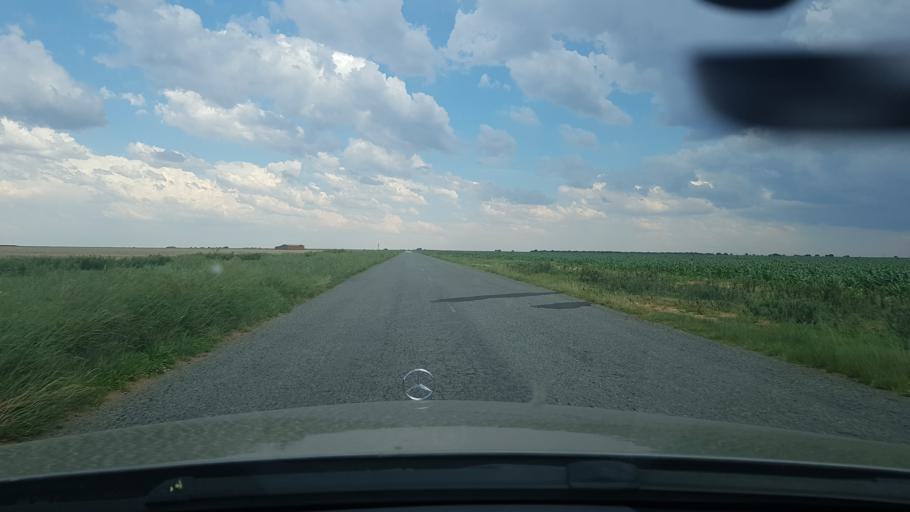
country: ZA
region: Orange Free State
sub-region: Lejweleputswa District Municipality
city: Hoopstad
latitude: -27.8883
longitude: 25.6680
